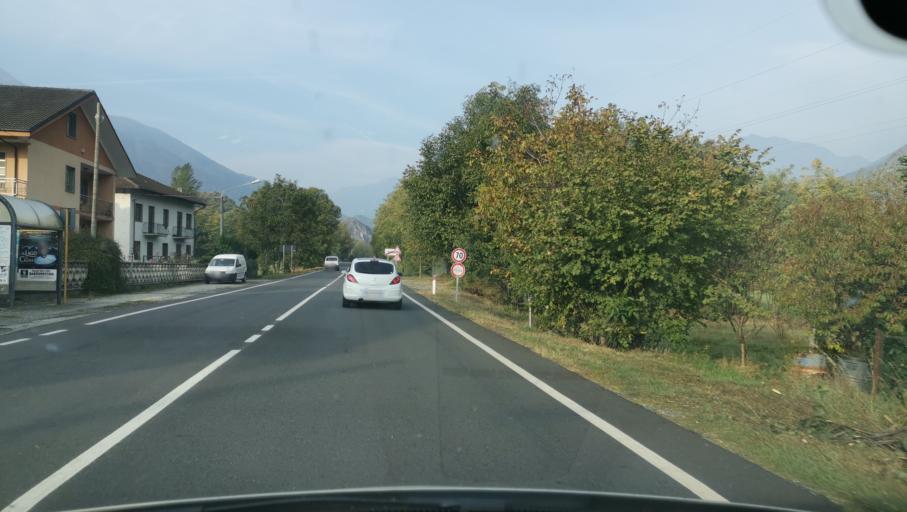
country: IT
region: Piedmont
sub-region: Provincia di Torino
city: Mattie
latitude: 45.1323
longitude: 7.1124
